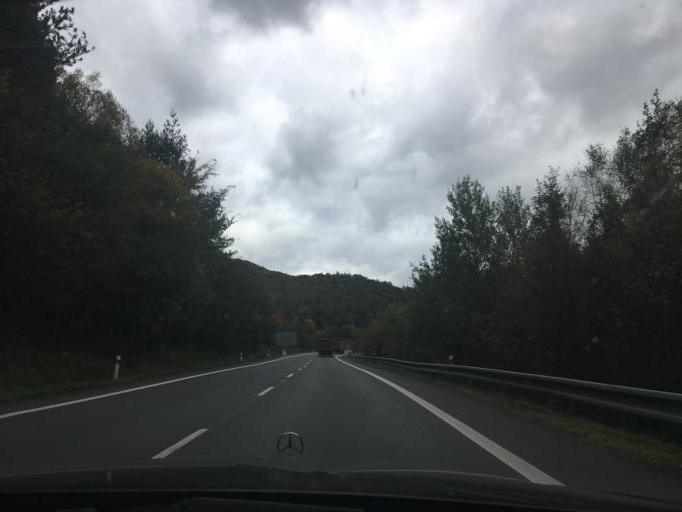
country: PL
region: Subcarpathian Voivodeship
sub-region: Powiat krosnienski
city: Jasliska
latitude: 49.3914
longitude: 21.6993
